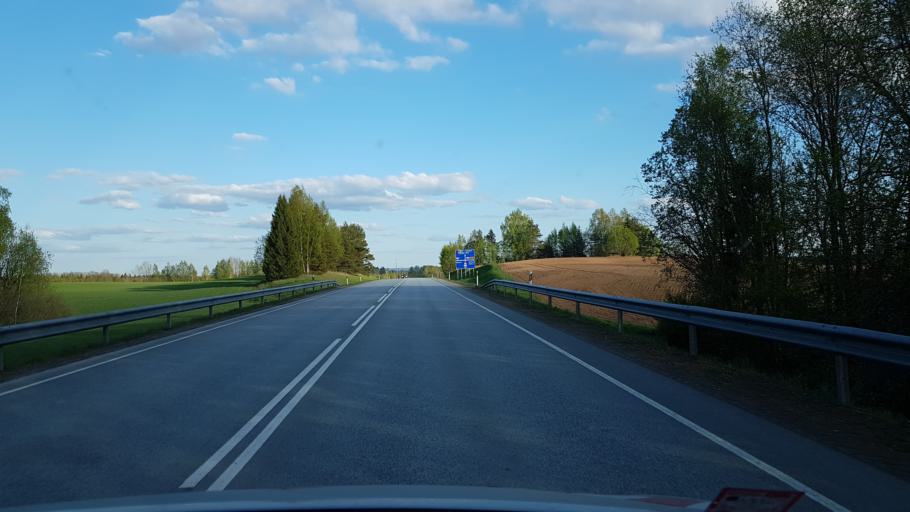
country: EE
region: Vorumaa
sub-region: Voru linn
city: Voru
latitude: 57.8949
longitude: 26.8451
